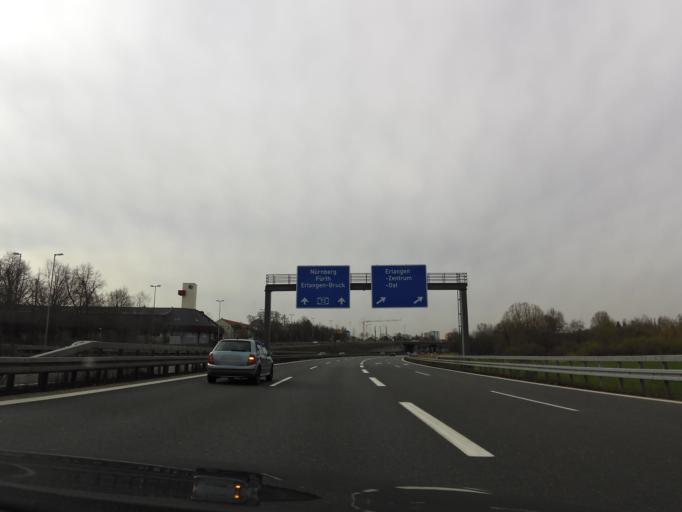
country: DE
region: Bavaria
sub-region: Regierungsbezirk Mittelfranken
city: Erlangen
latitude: 49.5944
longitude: 10.9980
